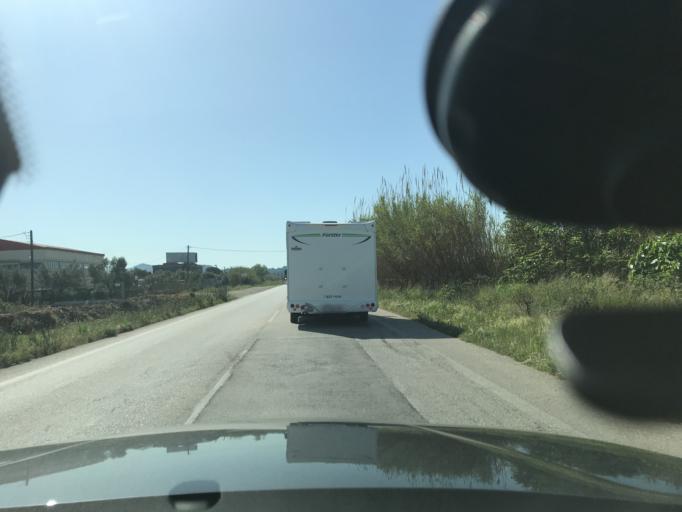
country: GR
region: West Greece
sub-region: Nomos Ileias
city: Pyrgos
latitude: 37.6567
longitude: 21.4654
